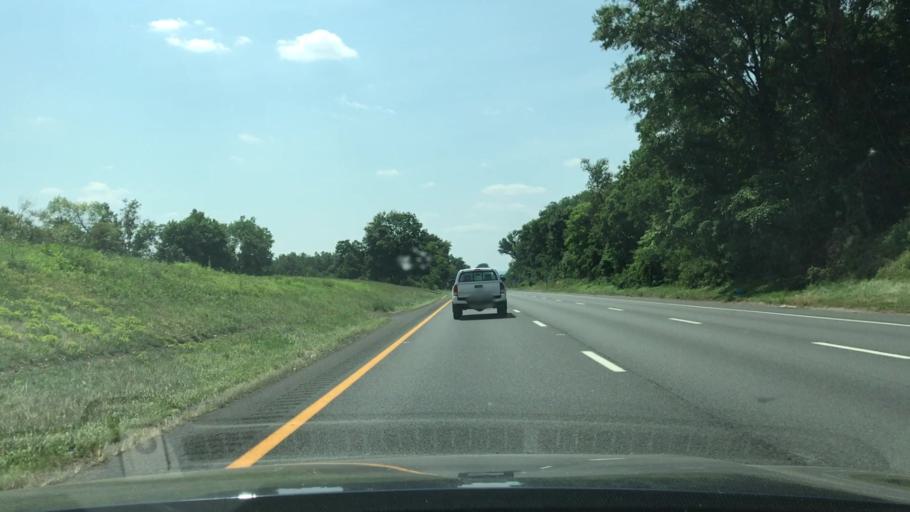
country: US
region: New Jersey
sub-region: Somerset County
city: Finderne
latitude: 40.5805
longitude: -74.5810
